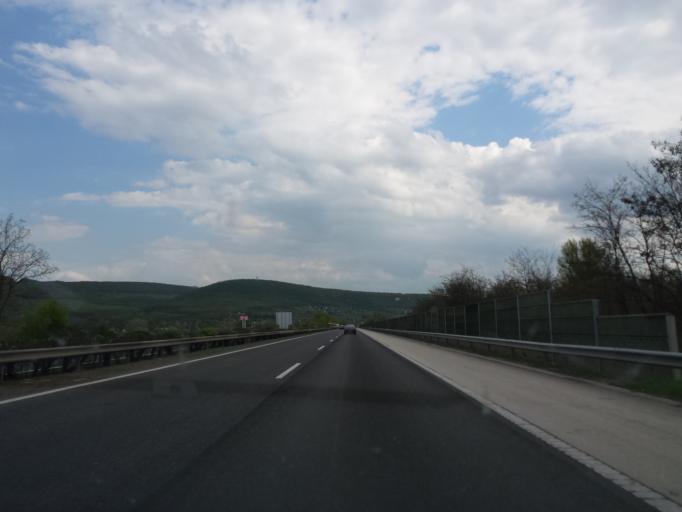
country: HU
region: Komarom-Esztergom
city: Vertesszolos
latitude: 47.6065
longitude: 18.3704
